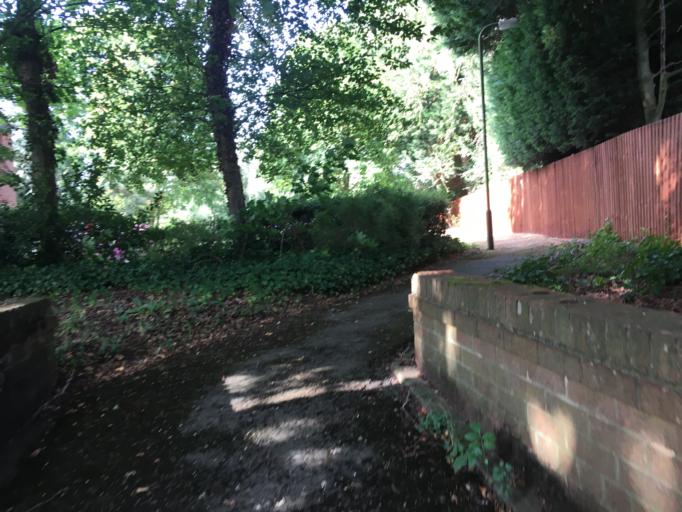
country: GB
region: England
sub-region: Warwickshire
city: Rugby
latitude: 52.3826
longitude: -1.2192
